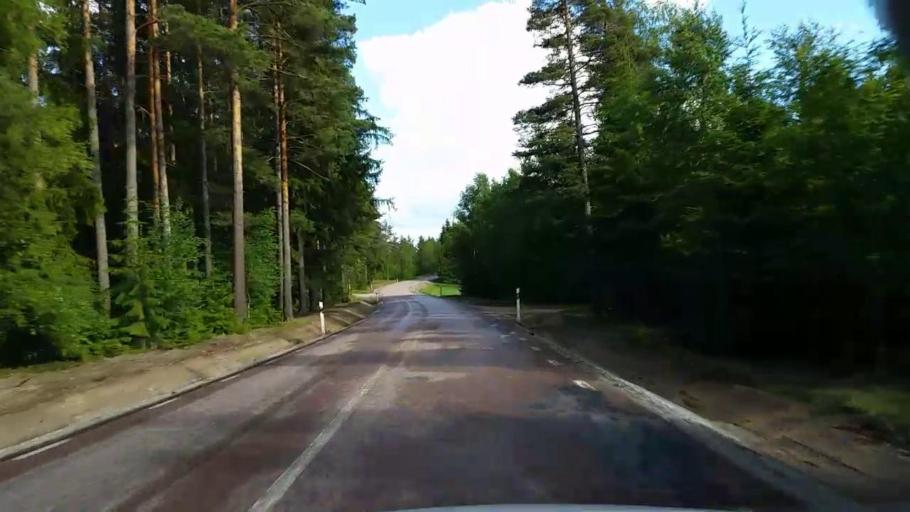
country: SE
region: Vaestmanland
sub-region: Fagersta Kommun
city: Fagersta
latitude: 59.8874
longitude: 15.8287
